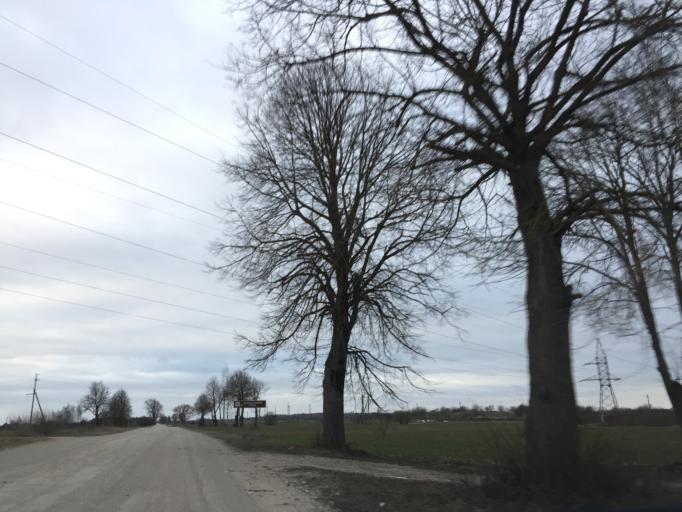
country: LT
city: Zagare
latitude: 56.3487
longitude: 23.2530
